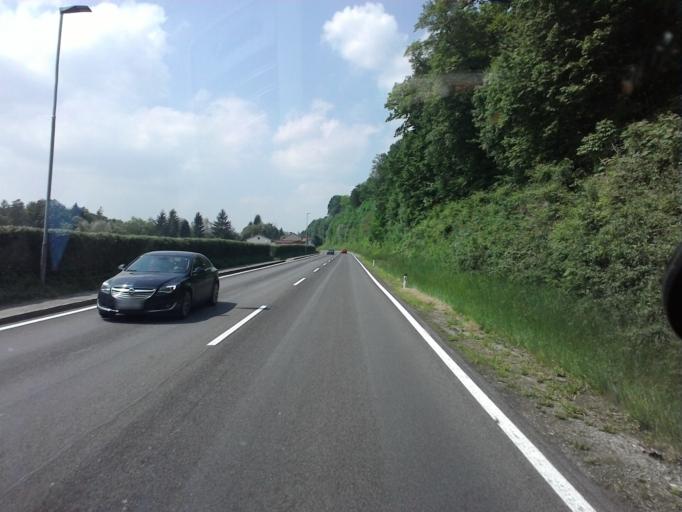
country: AT
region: Upper Austria
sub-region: Politischer Bezirk Steyr-Land
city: Garsten
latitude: 48.0471
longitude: 14.3720
